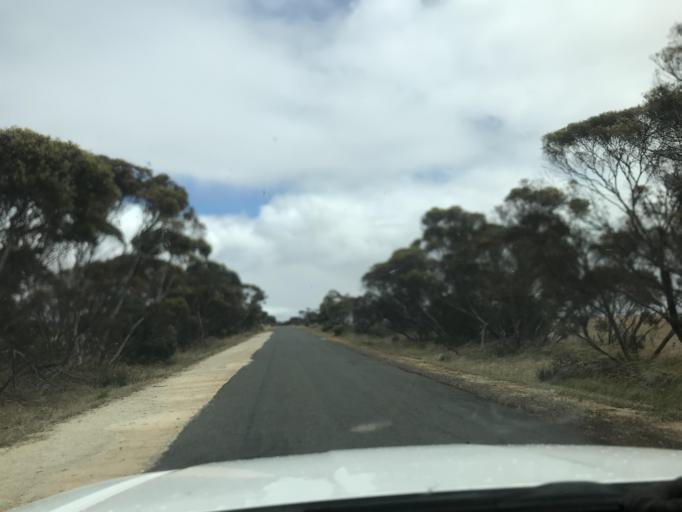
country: AU
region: South Australia
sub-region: Tatiara
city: Bordertown
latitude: -36.1434
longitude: 141.2286
